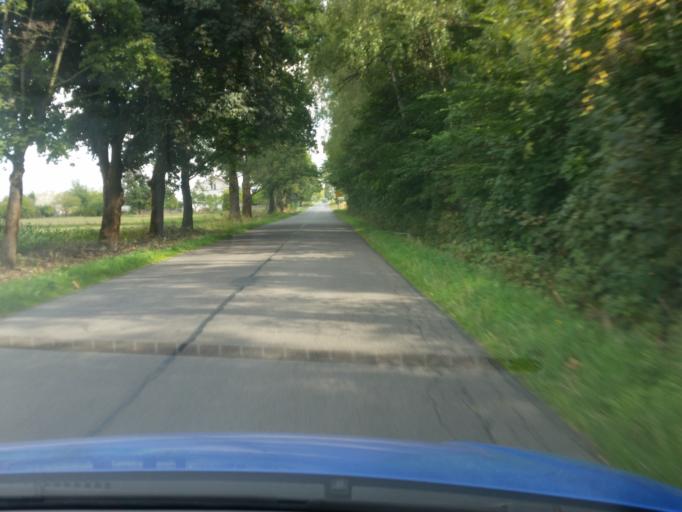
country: PL
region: Silesian Voivodeship
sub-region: Powiat czestochowski
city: Borowno
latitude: 50.9656
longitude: 19.3118
